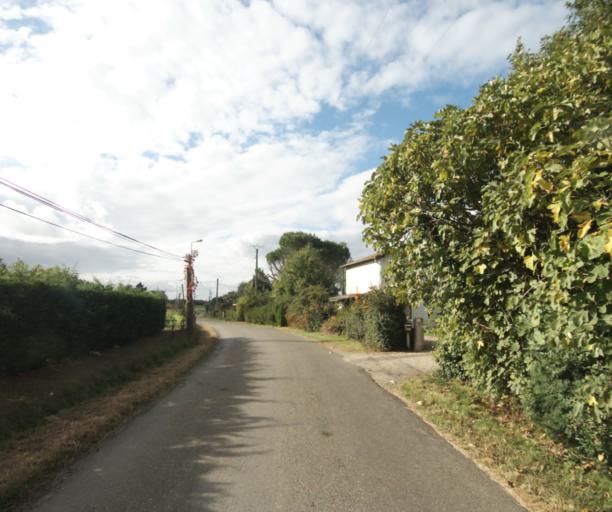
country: FR
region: Midi-Pyrenees
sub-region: Departement du Gers
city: Eauze
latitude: 43.8676
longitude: 0.0961
